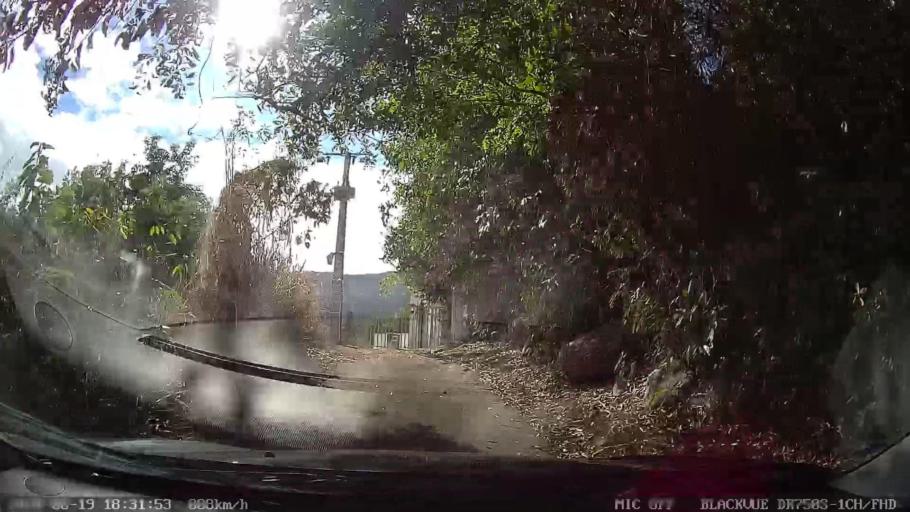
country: RE
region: Reunion
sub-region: Reunion
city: La Possession
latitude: -20.9587
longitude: 55.3512
